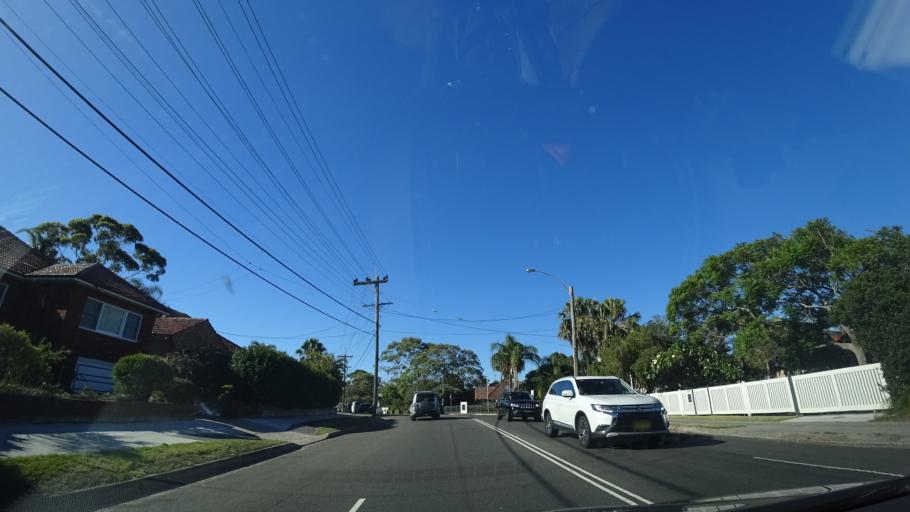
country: AU
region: New South Wales
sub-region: Warringah
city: Freshwater
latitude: -33.7720
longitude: 151.2793
